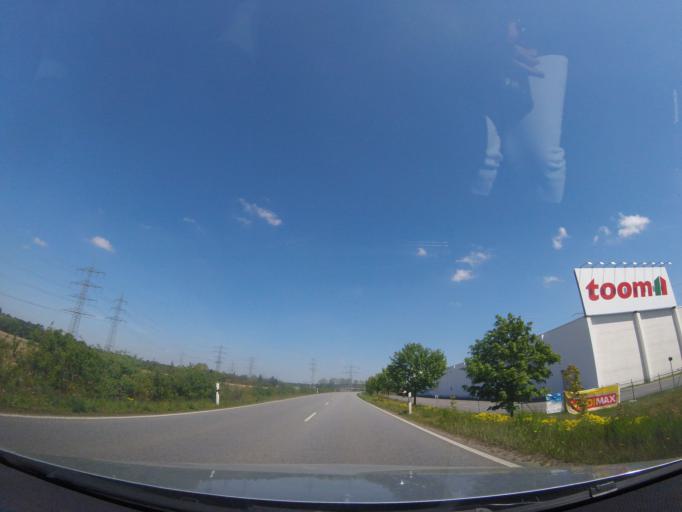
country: DE
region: Hesse
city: Pfungstadt
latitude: 49.8098
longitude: 8.5864
